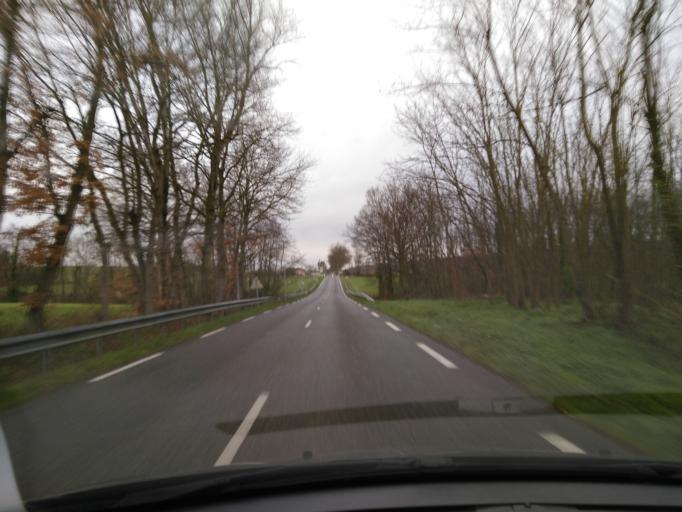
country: FR
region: Midi-Pyrenees
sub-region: Departement de la Haute-Garonne
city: Montesquieu-Volvestre
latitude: 43.1869
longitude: 1.2394
